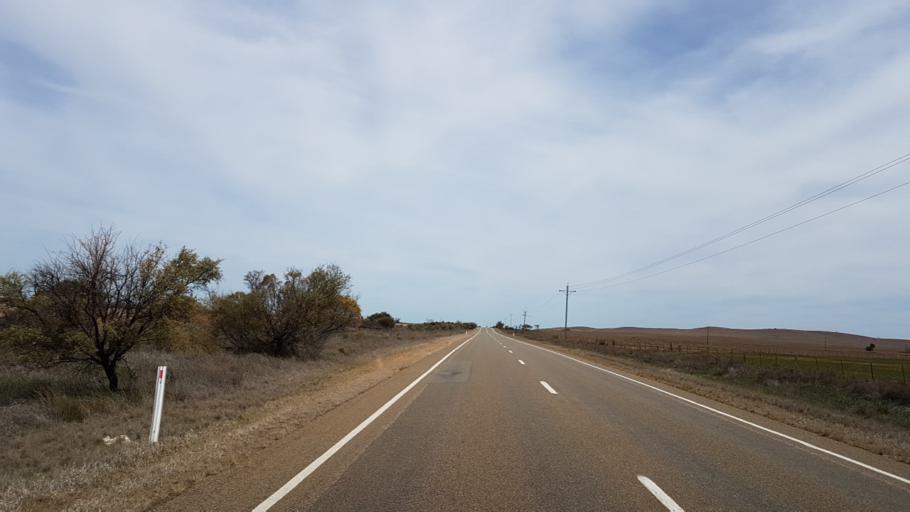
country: AU
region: South Australia
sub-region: Peterborough
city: Peterborough
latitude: -33.0072
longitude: 138.7694
